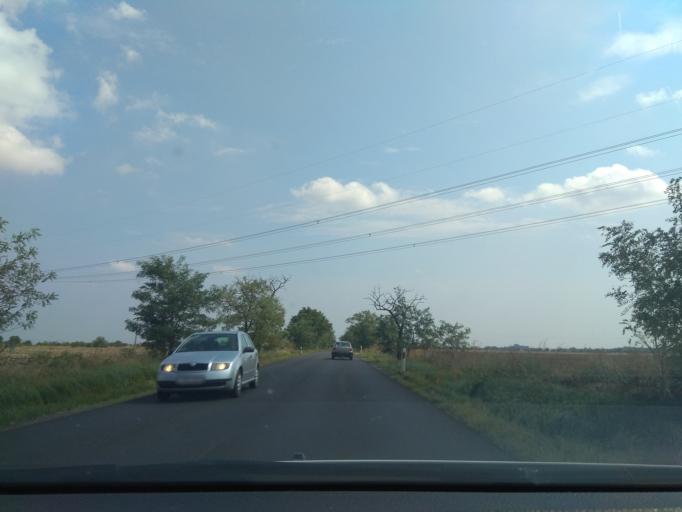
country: HU
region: Borsod-Abauj-Zemplen
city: Mezokovesd
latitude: 47.8137
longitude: 20.5281
